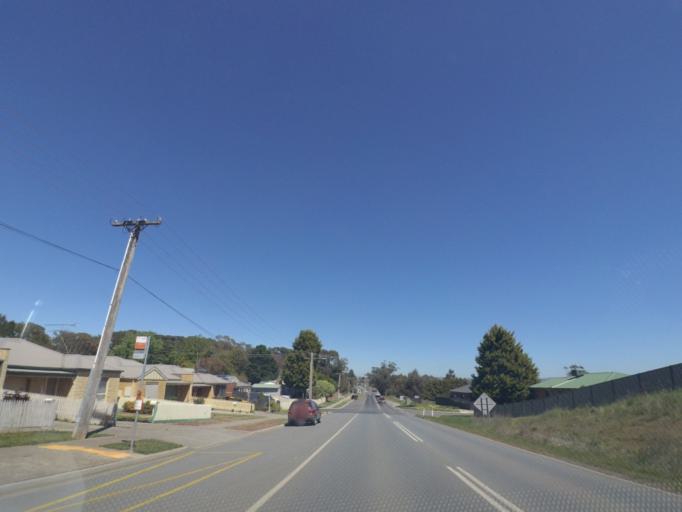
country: AU
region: Victoria
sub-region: Whittlesea
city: Whittlesea
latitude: -37.2893
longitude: 144.9565
